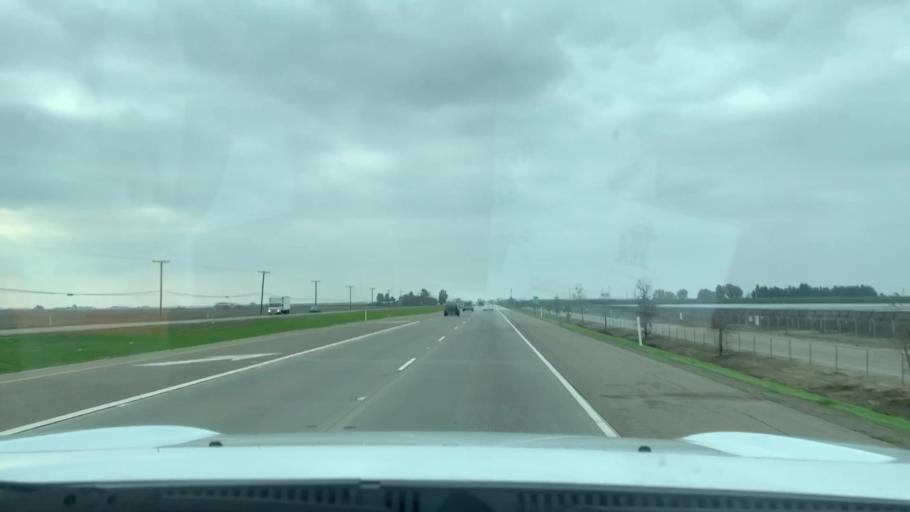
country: US
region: California
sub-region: Kings County
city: Home Garden
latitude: 36.3286
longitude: -119.5482
